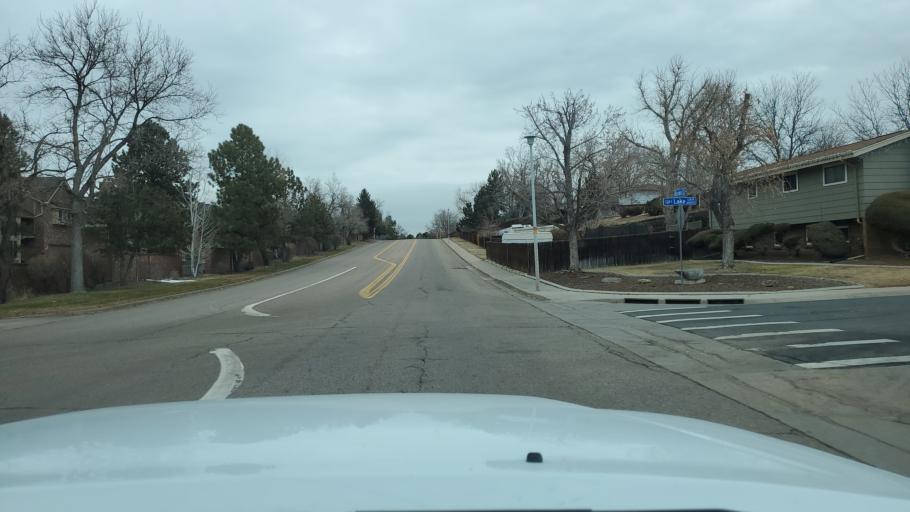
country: US
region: Colorado
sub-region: Arapahoe County
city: Greenwood Village
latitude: 39.6065
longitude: -104.9367
